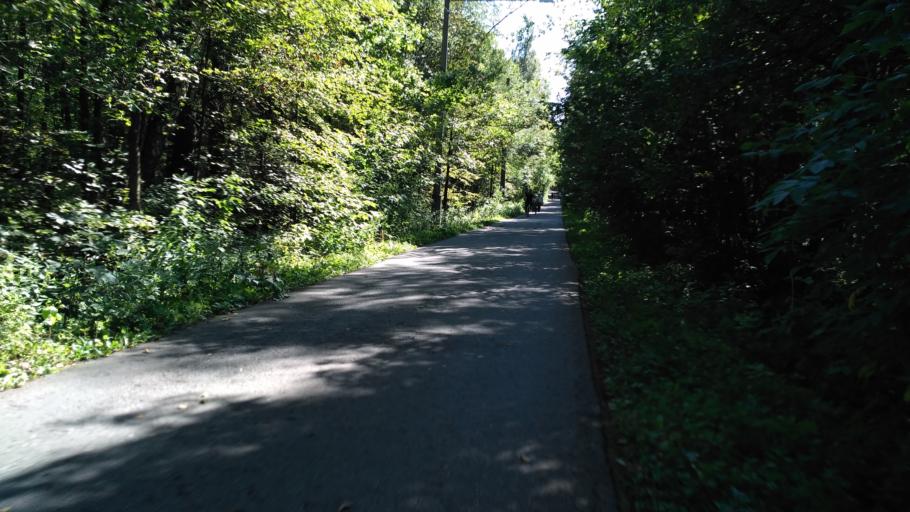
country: RU
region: Moscow
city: Metrogorodok
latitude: 55.7789
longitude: 37.7589
